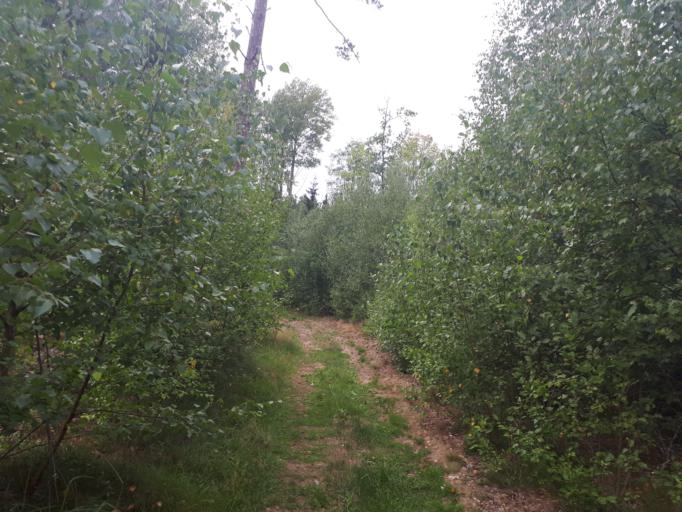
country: SE
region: Soedermanland
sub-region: Flens Kommun
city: Halleforsnas
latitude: 59.0705
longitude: 16.3898
